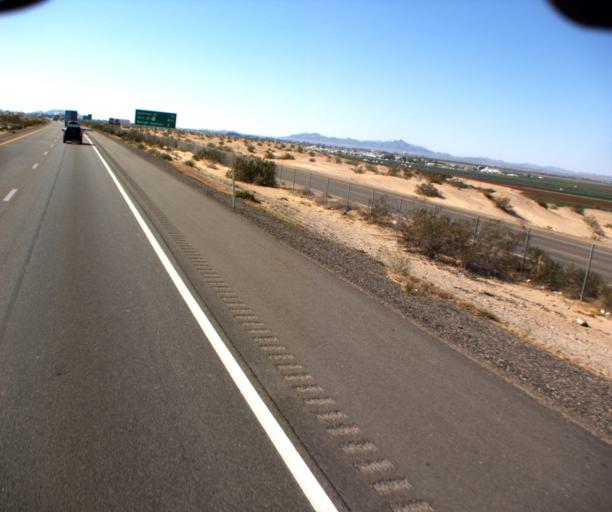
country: US
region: Arizona
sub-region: Yuma County
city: Yuma
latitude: 32.6863
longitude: -114.5680
